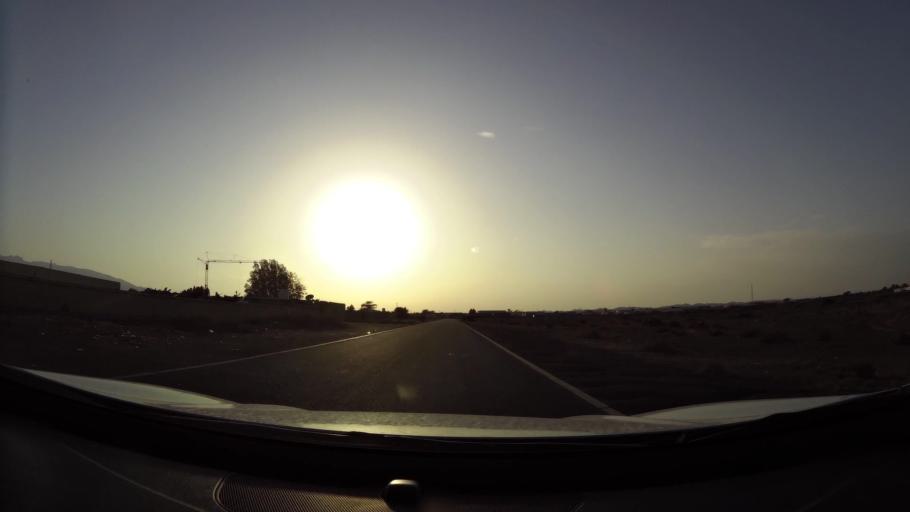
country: AE
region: Abu Dhabi
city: Al Ain
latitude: 24.1553
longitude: 55.8321
